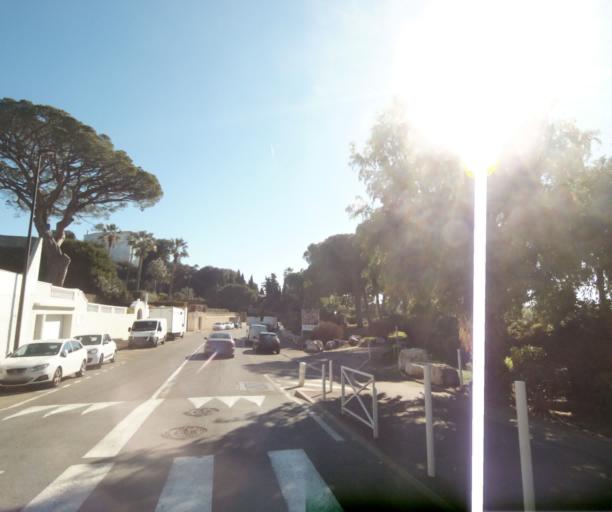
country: FR
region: Provence-Alpes-Cote d'Azur
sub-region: Departement des Alpes-Maritimes
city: Antibes
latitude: 43.5636
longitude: 7.1167
